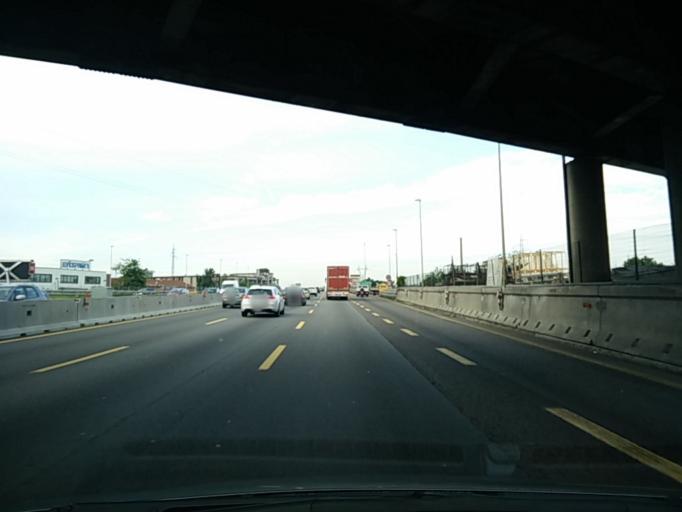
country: IT
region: Lombardy
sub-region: Citta metropolitana di Milano
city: Cormano
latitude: 45.5372
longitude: 9.1645
